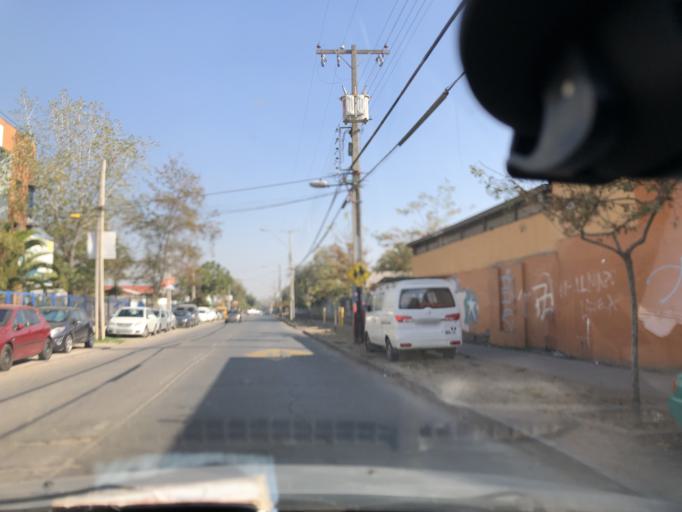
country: CL
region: Santiago Metropolitan
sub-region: Provincia de Cordillera
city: Puente Alto
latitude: -33.6093
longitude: -70.5799
